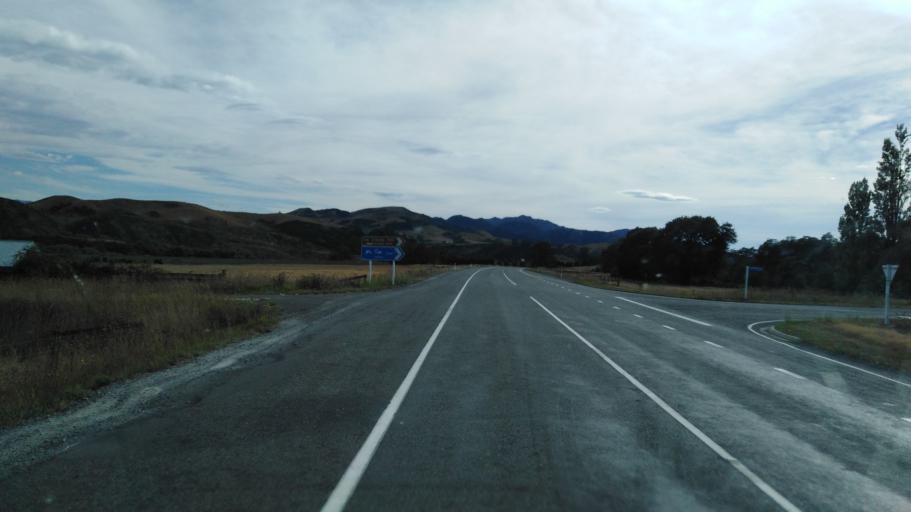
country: NZ
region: Canterbury
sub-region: Kaikoura District
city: Kaikoura
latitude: -42.6412
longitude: 173.3224
